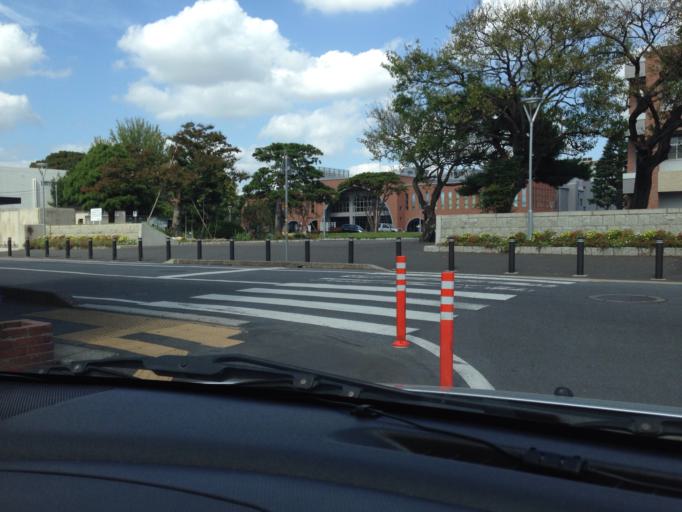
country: JP
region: Ibaraki
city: Mito-shi
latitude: 36.3999
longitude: 140.4423
